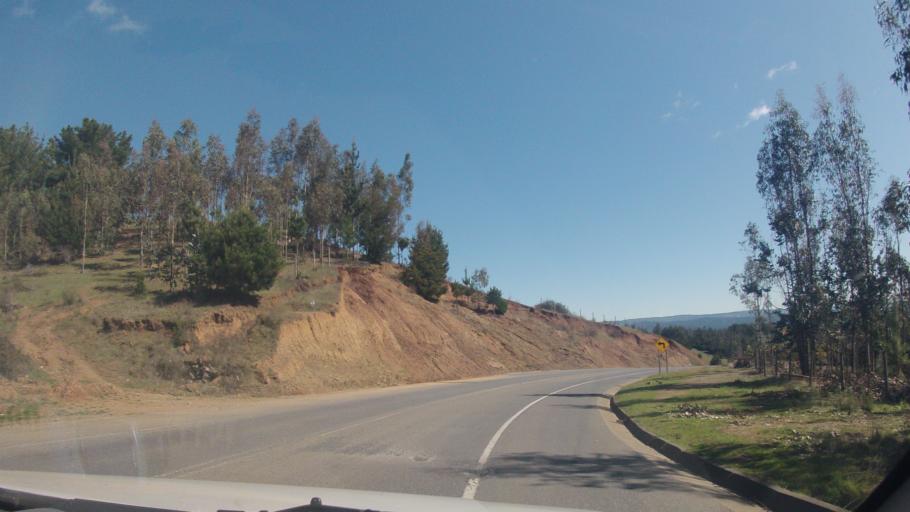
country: CL
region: Araucania
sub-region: Provincia de Malleco
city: Traiguen
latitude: -38.1722
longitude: -72.8681
